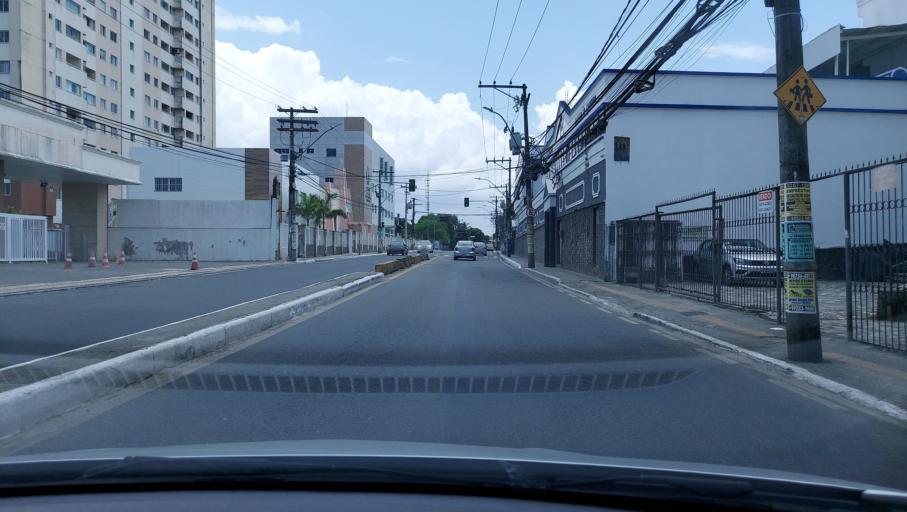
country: BR
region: Bahia
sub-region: Salvador
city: Salvador
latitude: -12.9651
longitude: -38.4726
